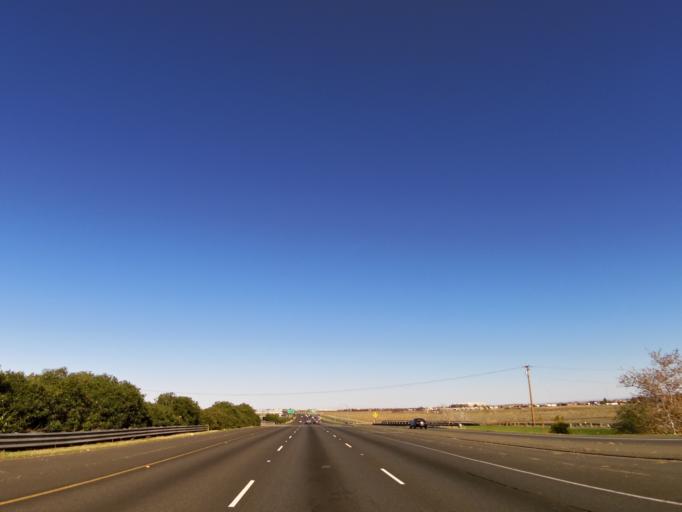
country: US
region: California
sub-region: Yolo County
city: West Sacramento
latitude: 38.6265
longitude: -121.5177
